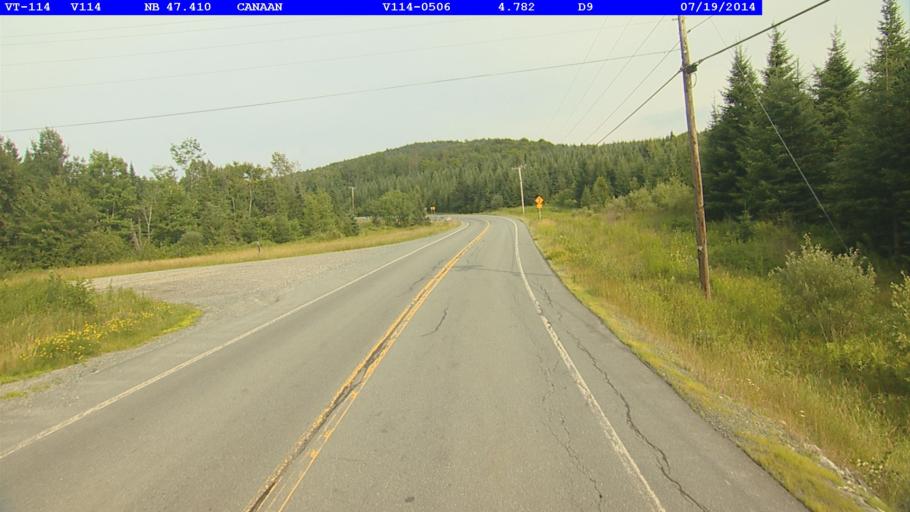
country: US
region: New Hampshire
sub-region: Coos County
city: Colebrook
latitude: 45.0066
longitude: -71.5988
